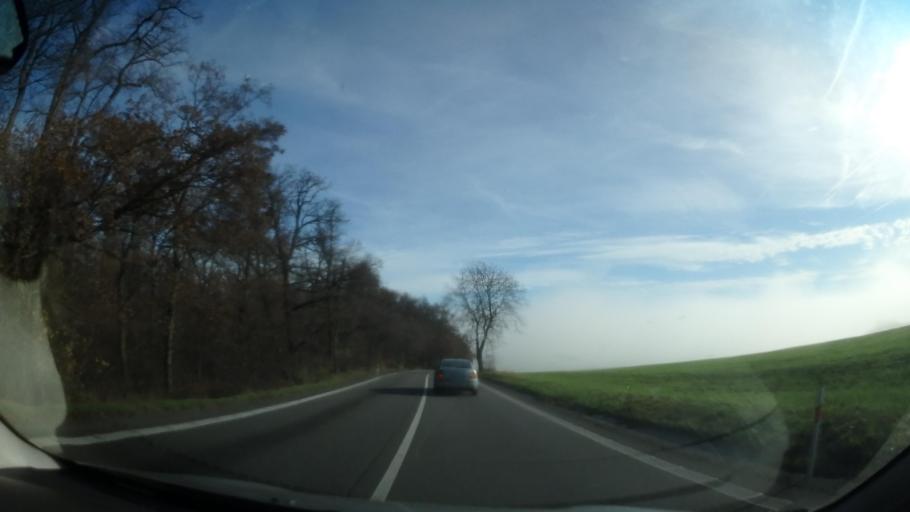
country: CZ
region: South Moravian
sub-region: Okres Hodonin
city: Kyjov
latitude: 49.0134
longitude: 17.0668
